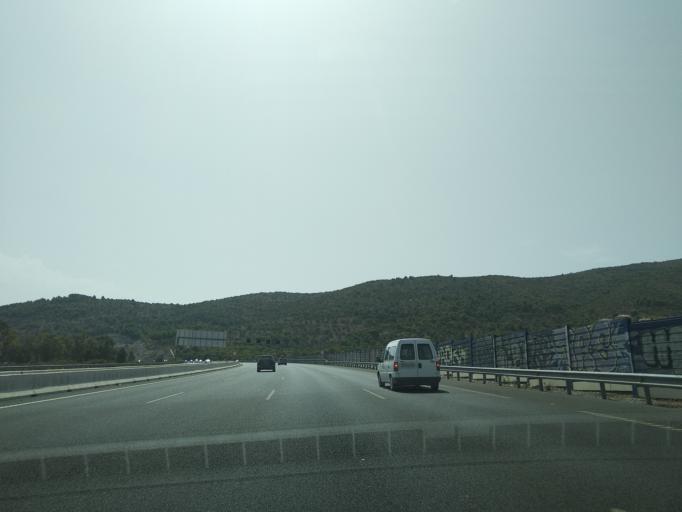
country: ES
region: Andalusia
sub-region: Provincia de Malaga
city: Alhaurin de la Torre
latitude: 36.6637
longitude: -4.5282
